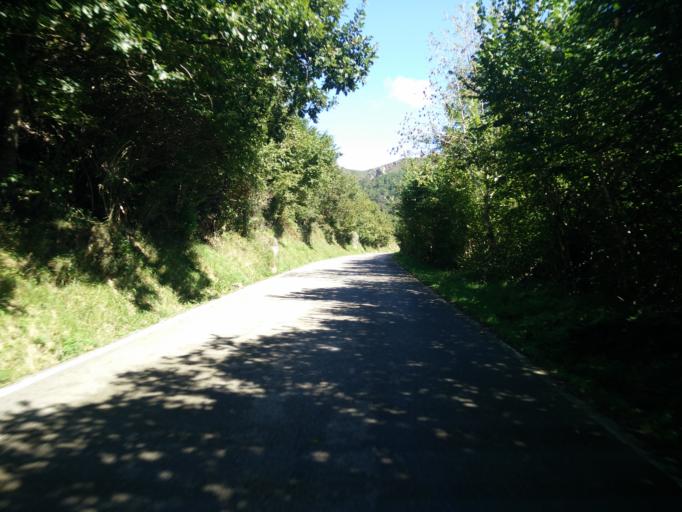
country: ES
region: Cantabria
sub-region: Provincia de Cantabria
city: Ruente
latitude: 43.1492
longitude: -4.2854
